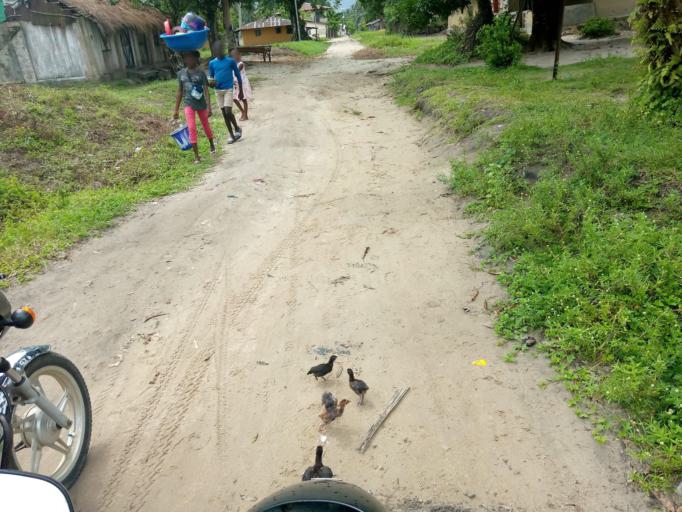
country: SL
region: Southern Province
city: Bonthe
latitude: 7.5285
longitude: -12.5042
